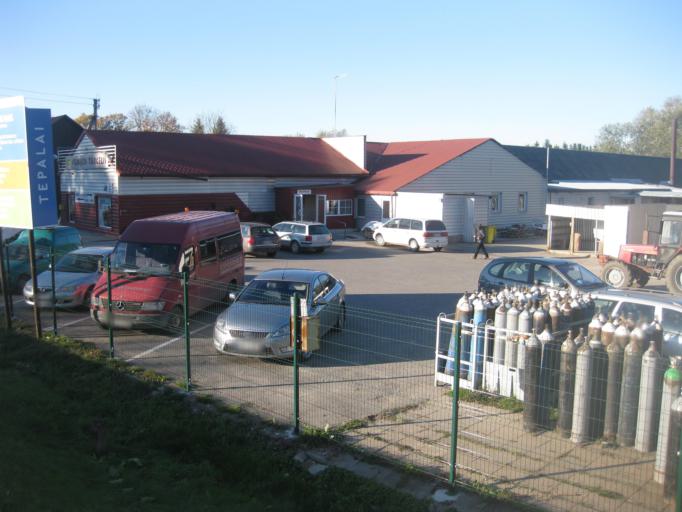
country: LT
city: Vilkija
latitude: 55.0427
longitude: 23.5871
